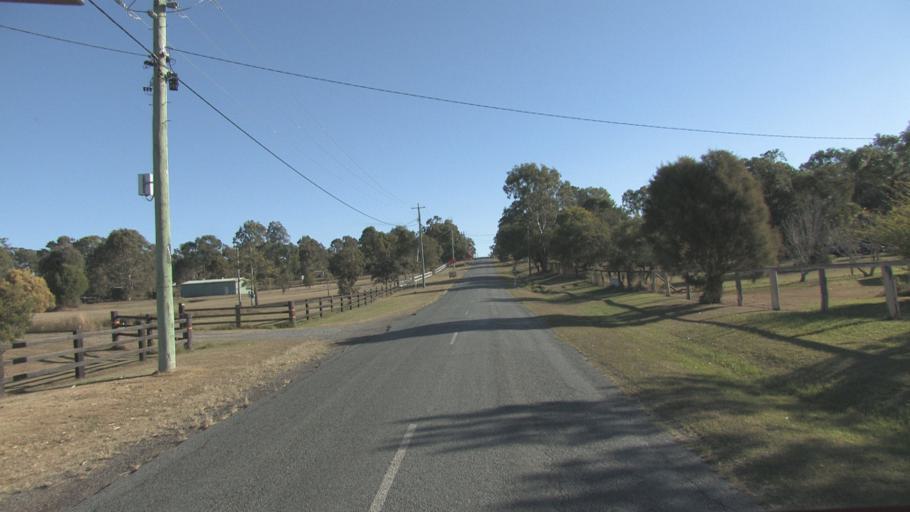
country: AU
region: Queensland
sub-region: Logan
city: Cedar Vale
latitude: -27.8307
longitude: 153.0082
